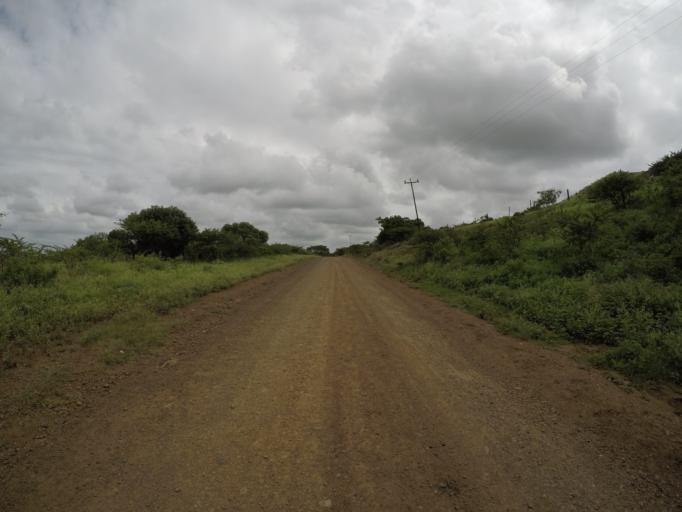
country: ZA
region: KwaZulu-Natal
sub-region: uThungulu District Municipality
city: Empangeni
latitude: -28.6097
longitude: 31.8969
